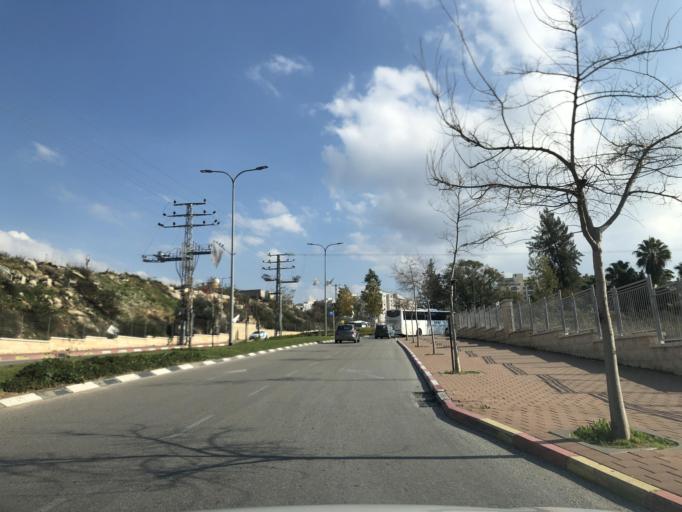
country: IL
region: Jerusalem
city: Modiin Ilit
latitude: 31.9356
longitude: 35.0466
